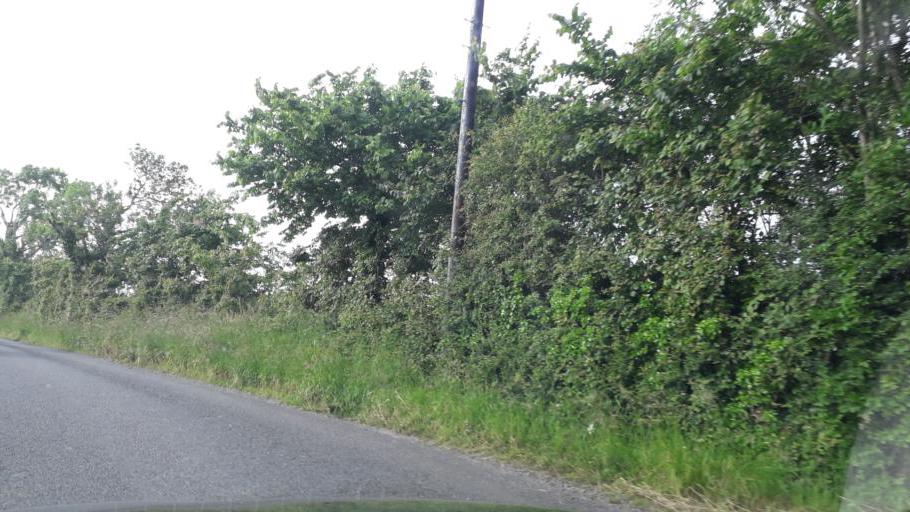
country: IE
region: Leinster
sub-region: Loch Garman
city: Courtown
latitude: 52.5432
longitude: -6.2529
